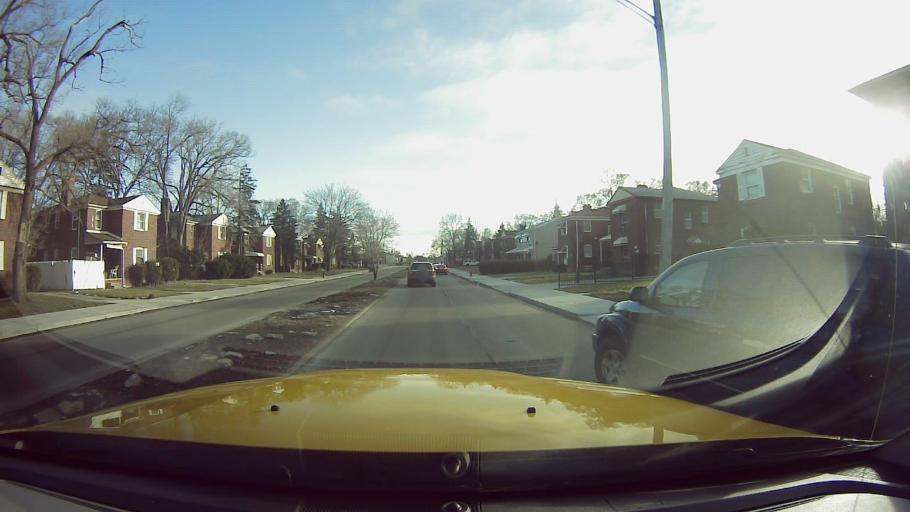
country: US
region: Michigan
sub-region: Wayne County
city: Highland Park
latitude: 42.3881
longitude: -83.1455
